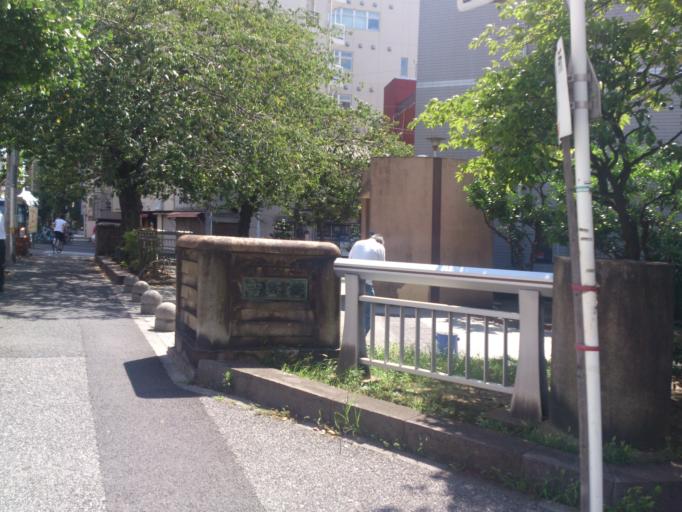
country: JP
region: Tokyo
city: Urayasu
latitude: 35.7193
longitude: 139.8018
